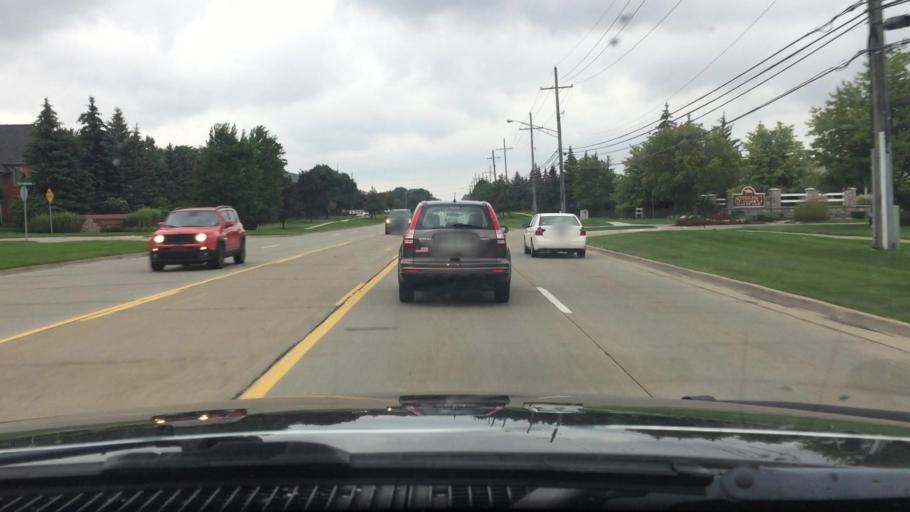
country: US
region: Michigan
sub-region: Macomb County
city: Utica
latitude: 42.6060
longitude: -83.0713
